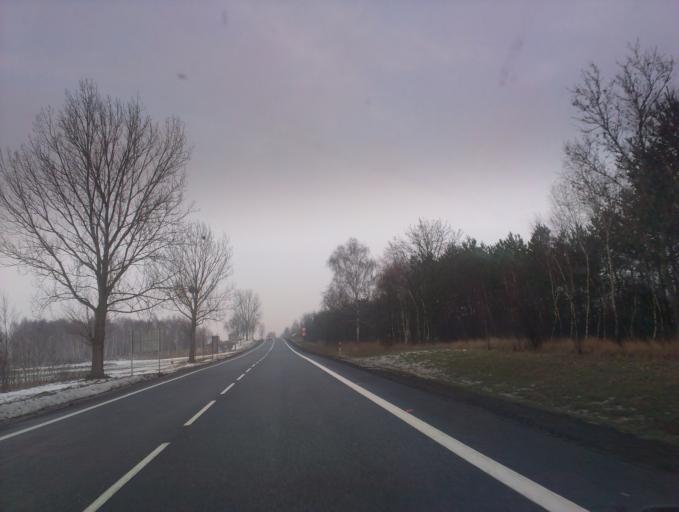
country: PL
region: Greater Poland Voivodeship
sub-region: Powiat poznanski
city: Zlotniki
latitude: 52.5410
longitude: 16.8383
